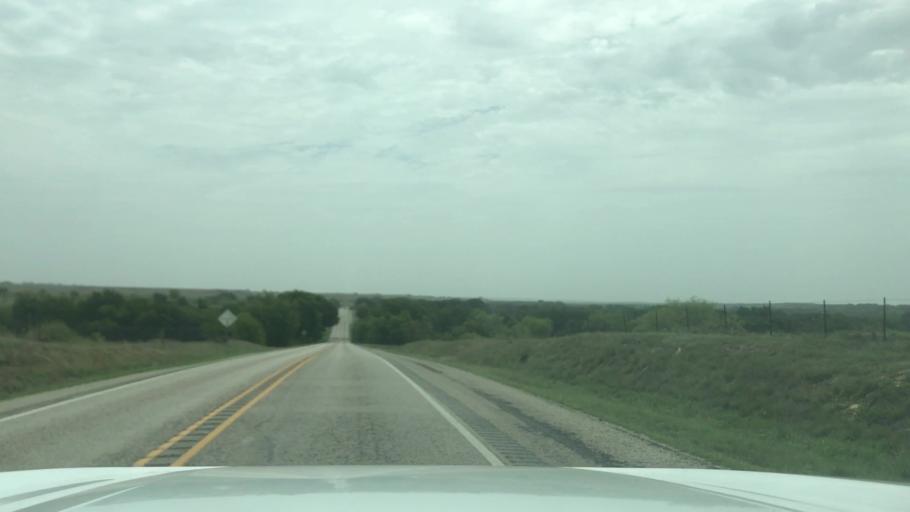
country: US
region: Texas
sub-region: Erath County
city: Dublin
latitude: 32.0579
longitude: -98.1997
